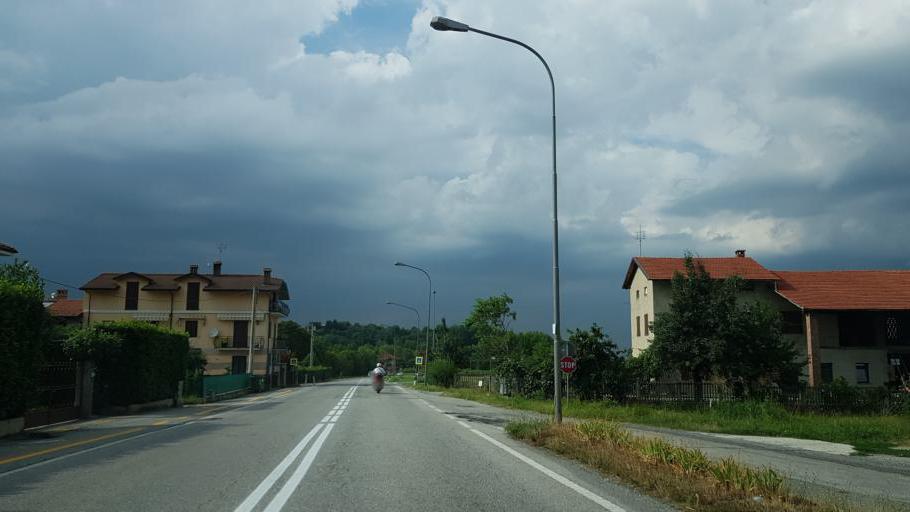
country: IT
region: Piedmont
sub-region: Provincia di Cuneo
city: Vignolo
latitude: 44.3637
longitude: 7.4748
